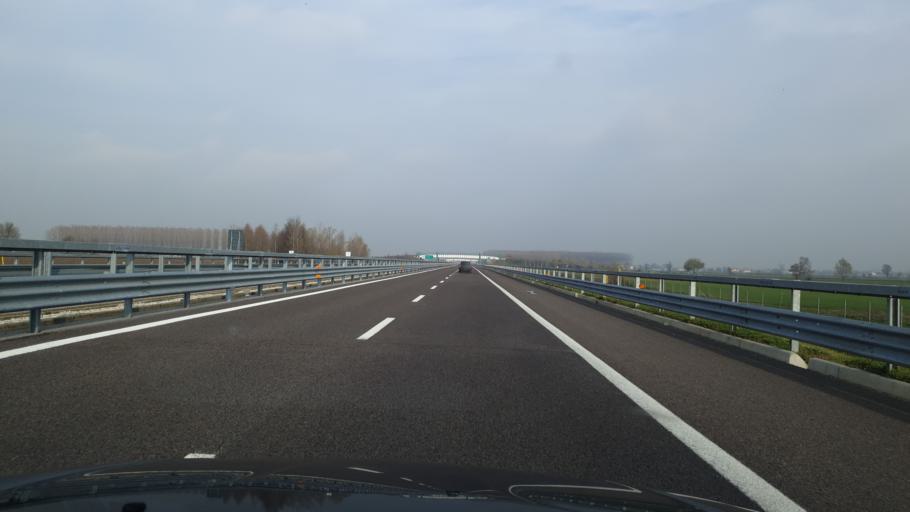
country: IT
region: Veneto
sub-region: Provincia di Padova
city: Megliadino San Vitale
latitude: 45.1800
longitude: 11.5371
